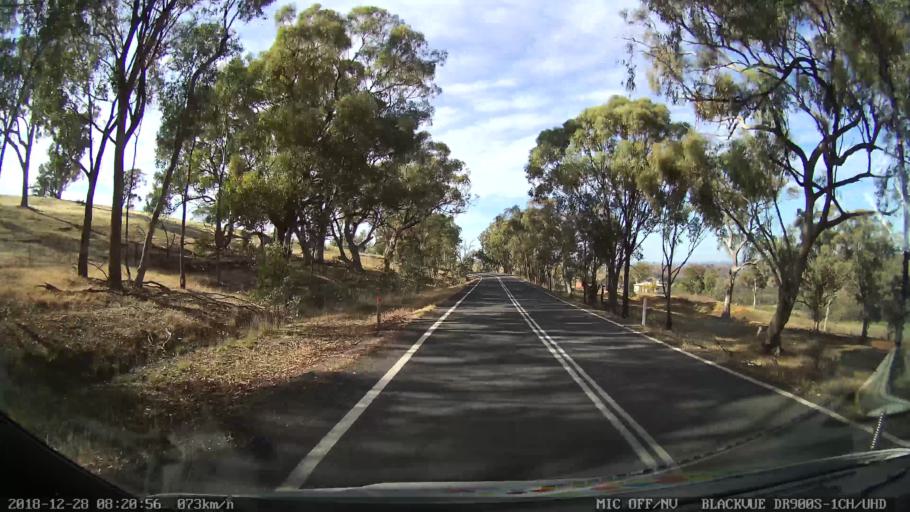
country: AU
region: New South Wales
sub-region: Blayney
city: Blayney
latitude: -33.8770
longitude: 149.3507
